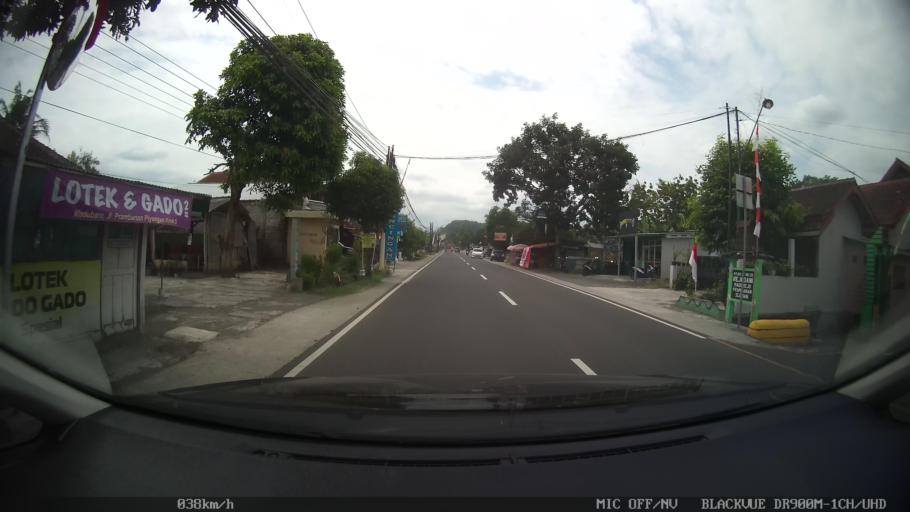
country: ID
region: Central Java
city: Candi Prambanan
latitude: -7.7859
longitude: 110.4827
